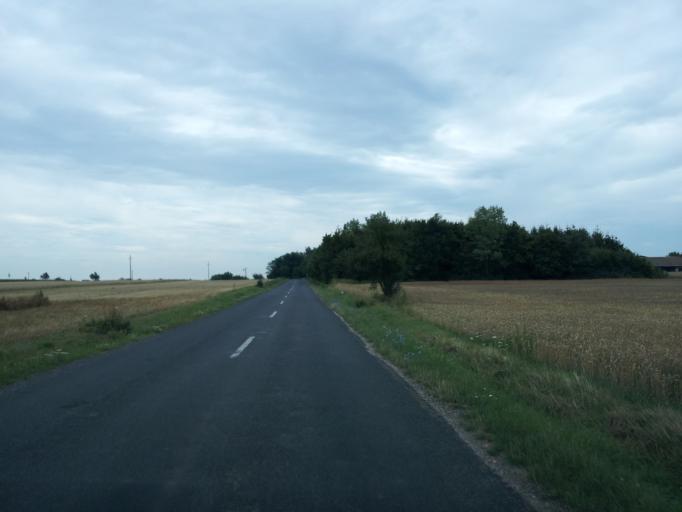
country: HU
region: Vas
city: Vasvar
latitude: 46.9737
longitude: 16.7274
